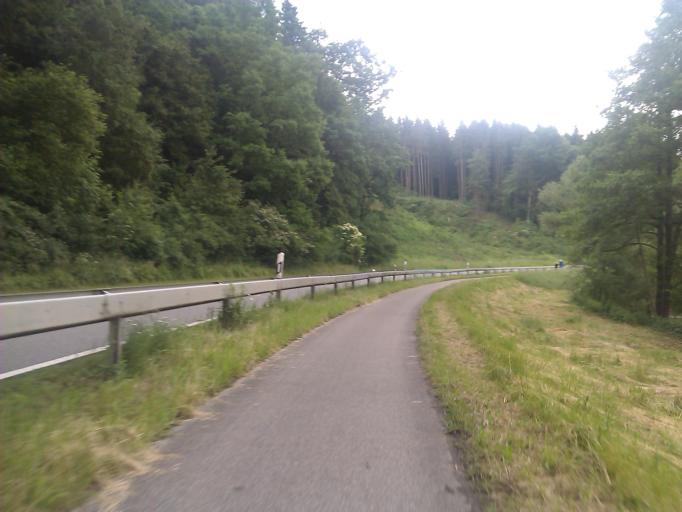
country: DE
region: Baden-Wuerttemberg
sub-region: Regierungsbezirk Stuttgart
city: Abtsgmund
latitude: 48.9039
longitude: 9.9920
